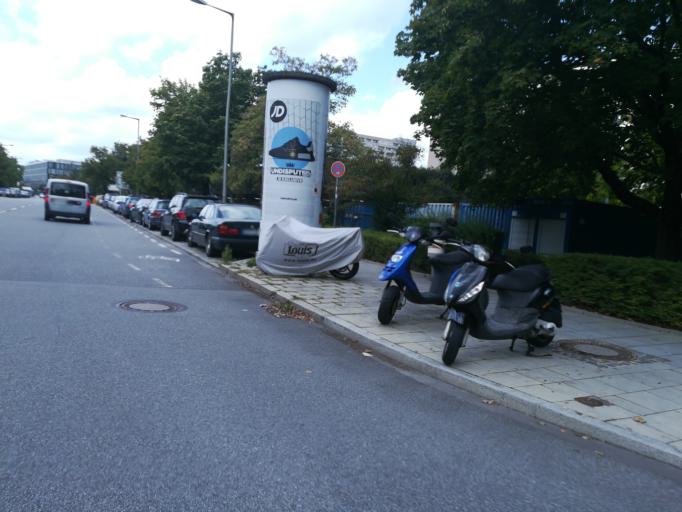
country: DE
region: Bavaria
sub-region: Upper Bavaria
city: Munich
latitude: 48.1819
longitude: 11.5366
